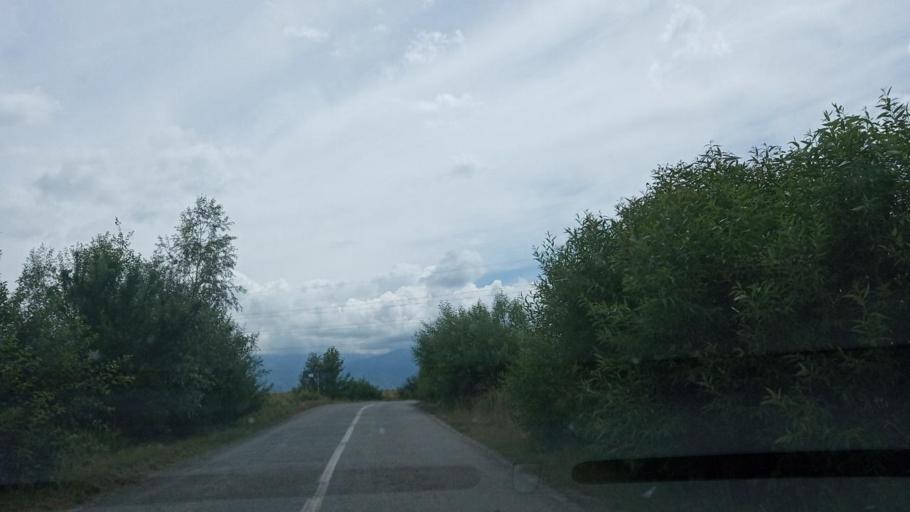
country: RO
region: Sibiu
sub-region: Comuna Porumbacu de Jos
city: Porumbacu de Jos
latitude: 45.7485
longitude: 24.4625
